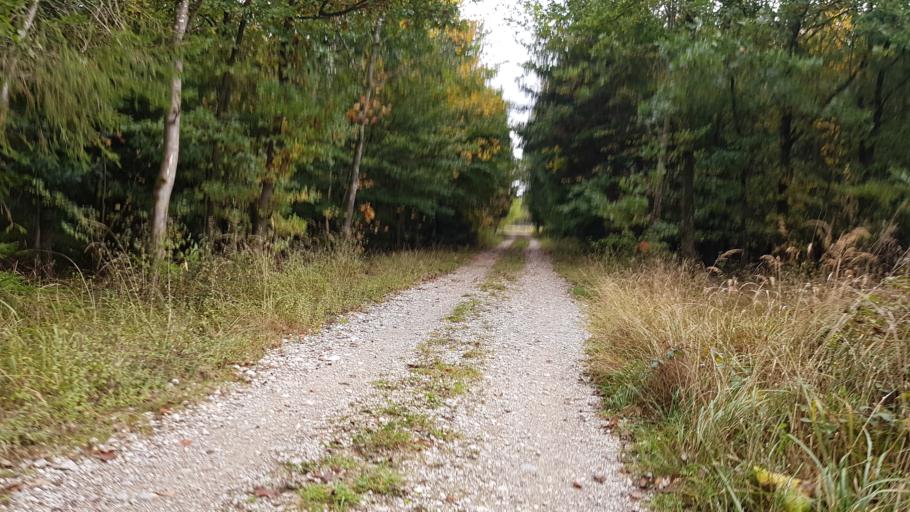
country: DE
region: Bavaria
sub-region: Upper Bavaria
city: Germering
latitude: 48.1050
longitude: 11.3501
